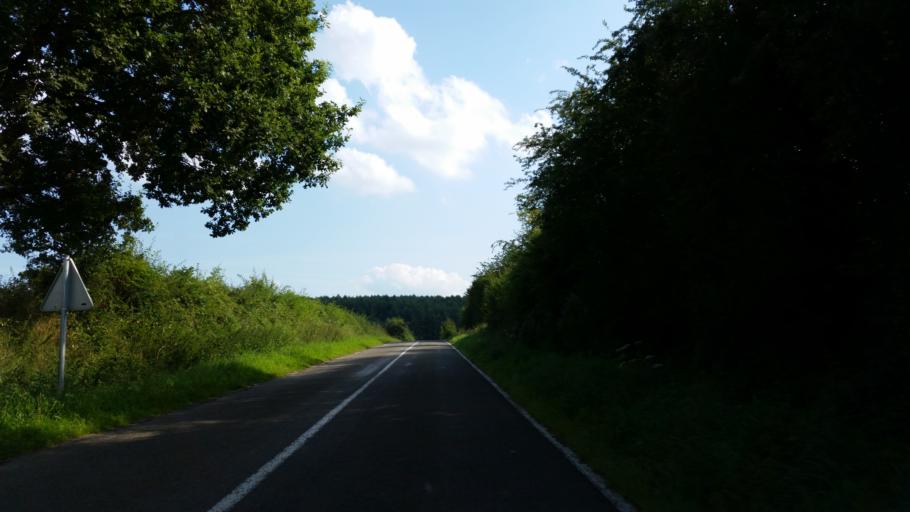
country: BE
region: Wallonia
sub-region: Province du Luxembourg
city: Durbuy
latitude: 50.3923
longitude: 5.4441
